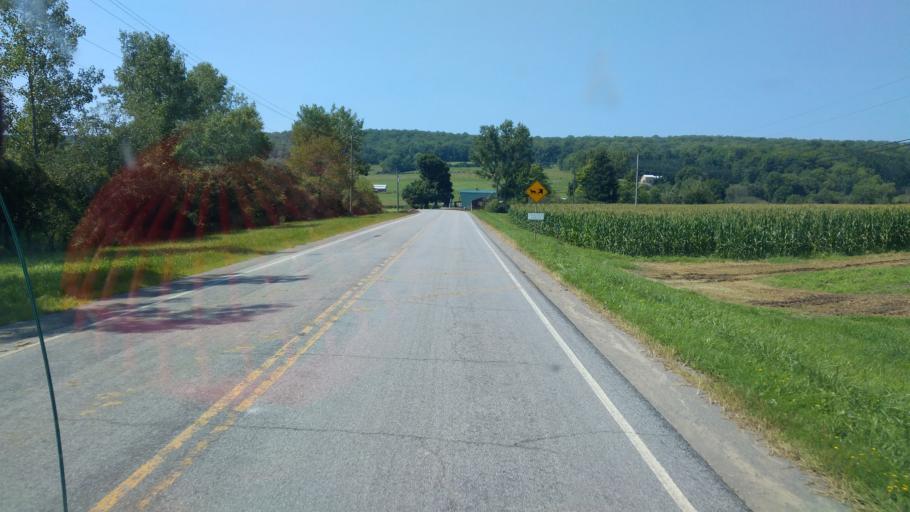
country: US
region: New York
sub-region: Allegany County
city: Belmont
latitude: 42.3220
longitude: -77.9444
